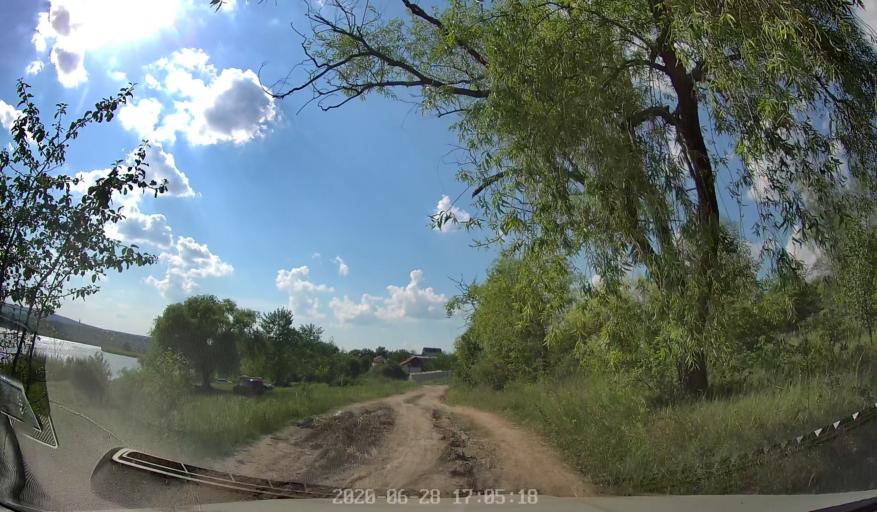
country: MD
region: Laloveni
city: Ialoveni
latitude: 46.9836
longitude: 28.7019
